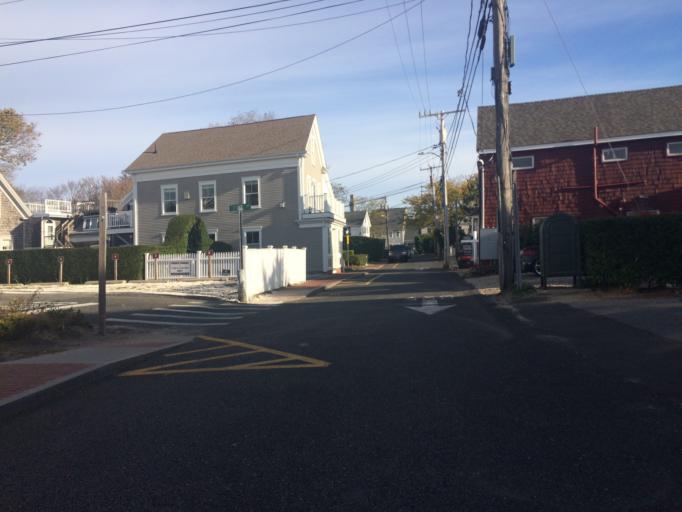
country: US
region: Massachusetts
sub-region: Barnstable County
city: Provincetown
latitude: 42.0438
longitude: -70.1924
